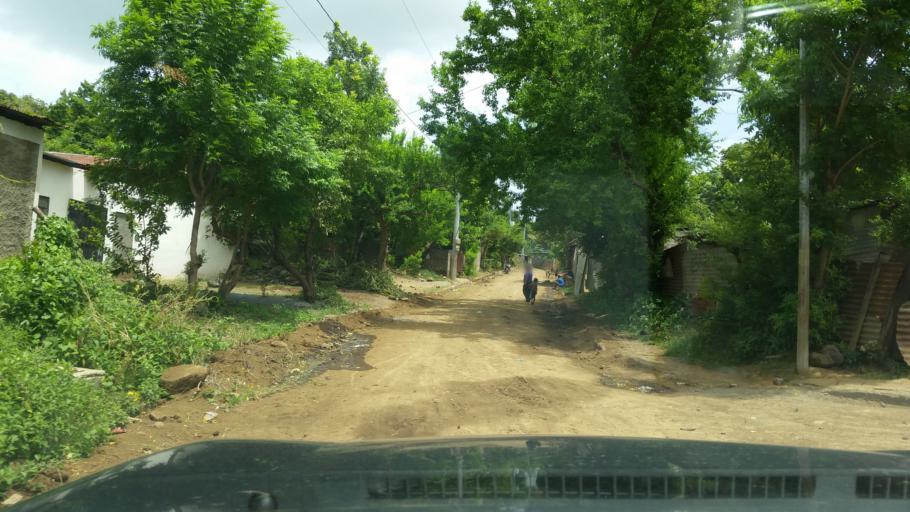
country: NI
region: Managua
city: Managua
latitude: 12.1157
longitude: -86.2211
